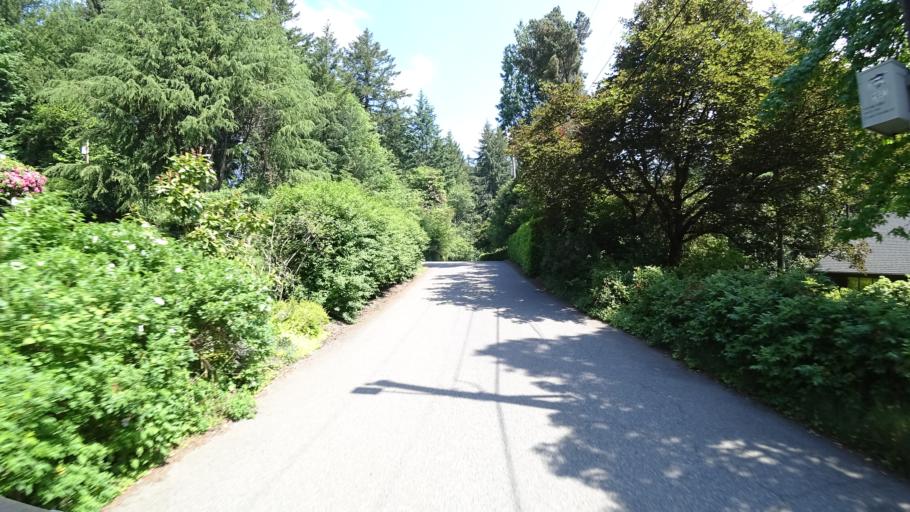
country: US
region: Oregon
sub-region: Washington County
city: West Haven-Sylvan
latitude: 45.5203
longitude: -122.7275
